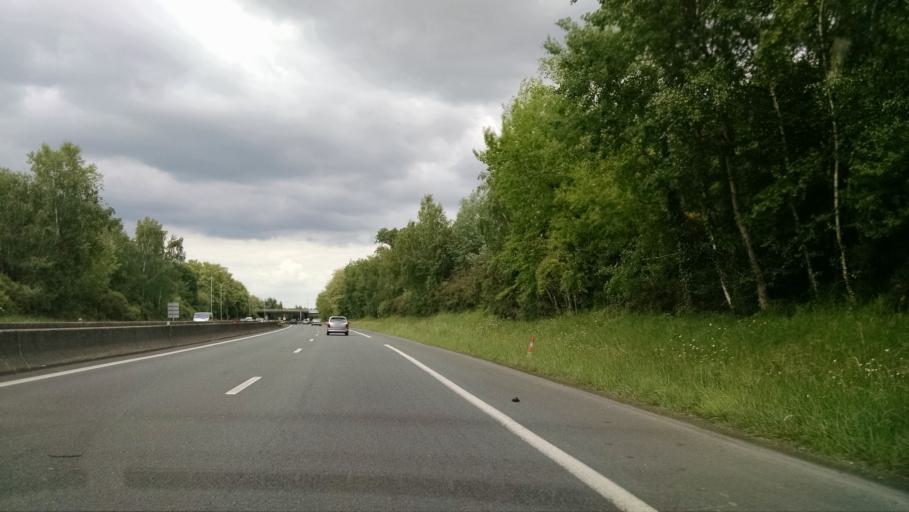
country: FR
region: Pays de la Loire
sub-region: Departement de la Loire-Atlantique
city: Basse-Goulaine
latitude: 47.2062
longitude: -1.4838
